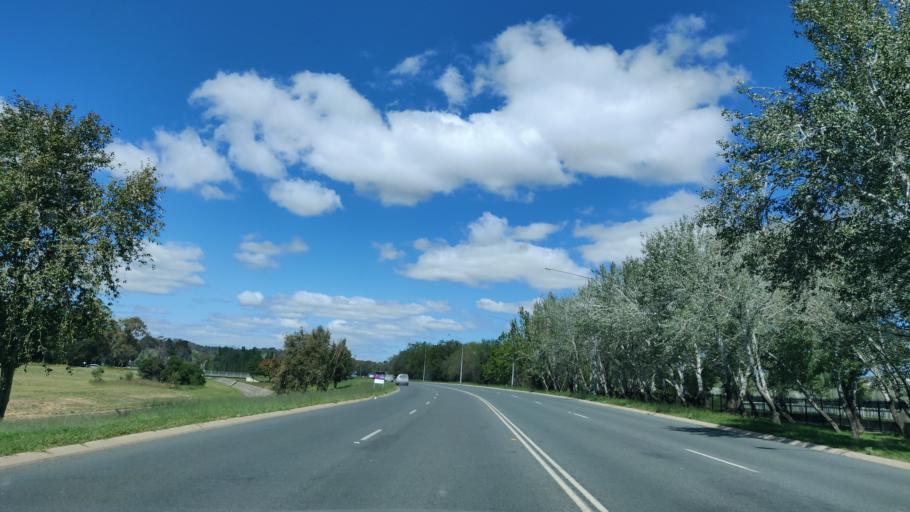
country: AU
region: Australian Capital Territory
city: Forrest
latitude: -35.3594
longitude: 149.0917
